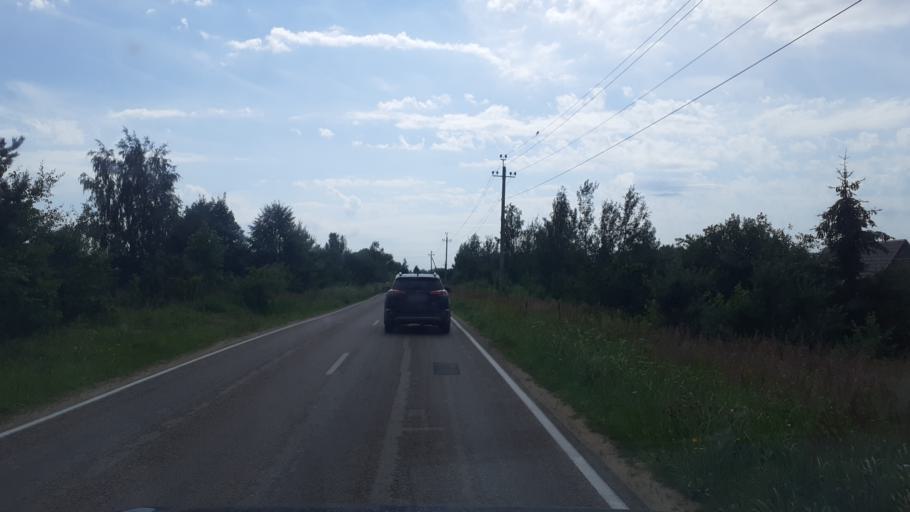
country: RU
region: Moskovskaya
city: Chupryakovo
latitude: 55.5638
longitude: 36.5678
